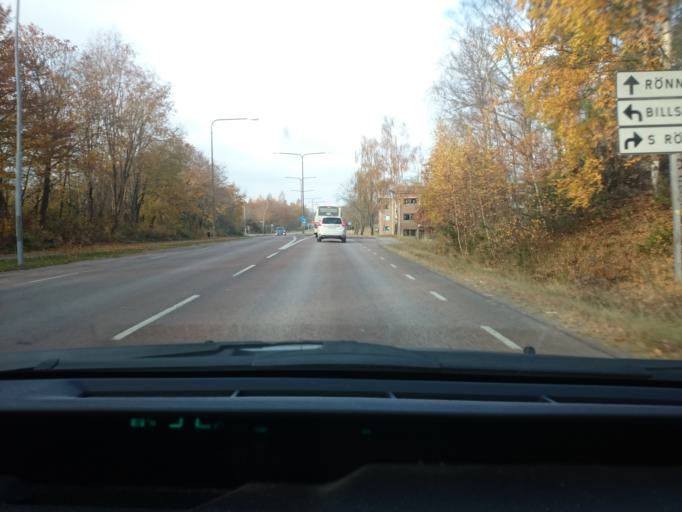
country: SE
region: Vaestmanland
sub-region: Vasteras
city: Vasteras
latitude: 59.6397
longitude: 16.5084
